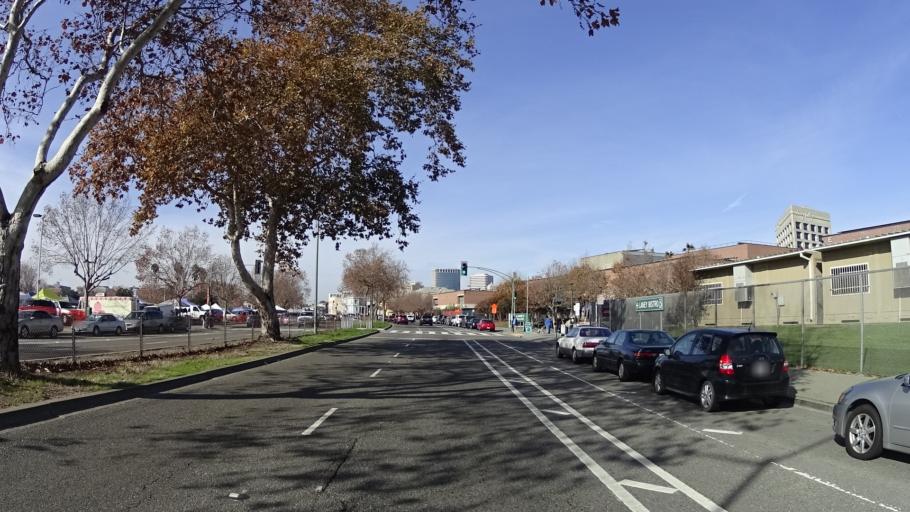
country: US
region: California
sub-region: Alameda County
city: Oakland
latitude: 37.7947
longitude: -122.2625
